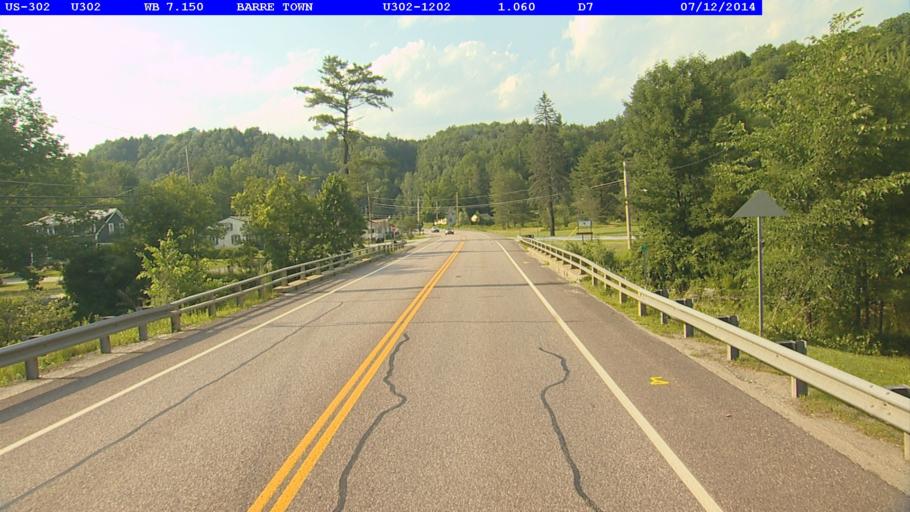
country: US
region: Vermont
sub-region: Washington County
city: South Barre
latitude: 44.1758
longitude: -72.4686
